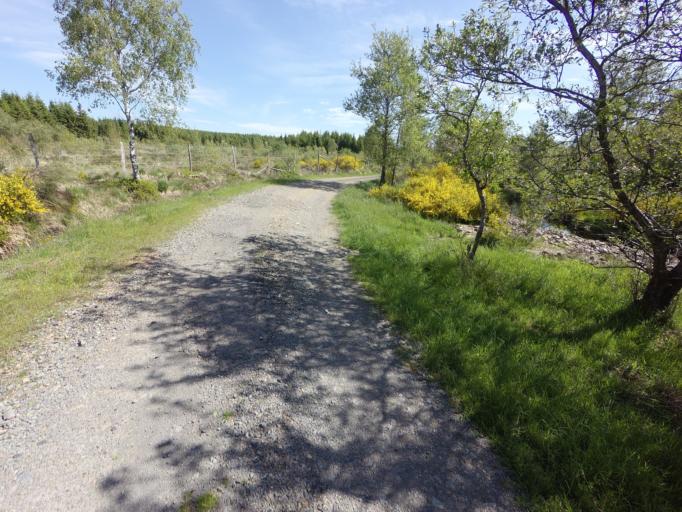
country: BE
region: Wallonia
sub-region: Province de Liege
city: Malmedy
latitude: 50.4989
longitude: 6.0265
